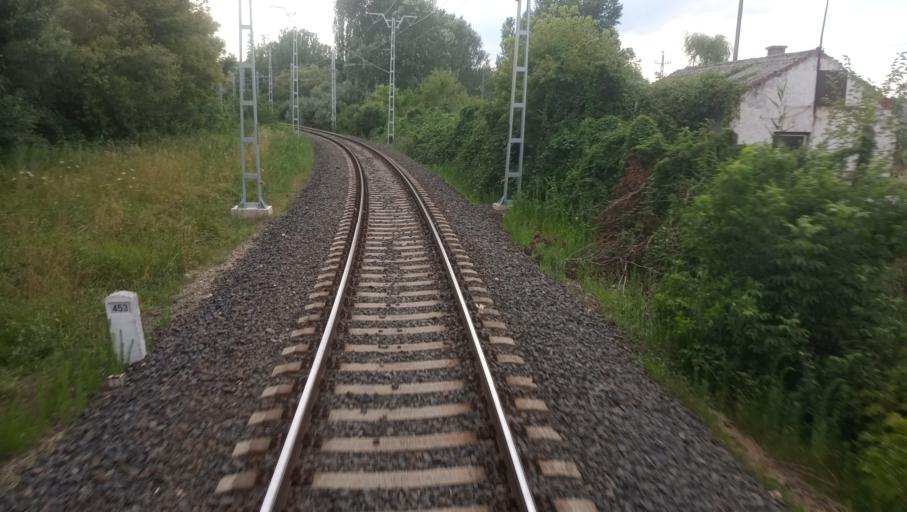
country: HU
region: Veszprem
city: Balatonalmadi
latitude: 47.0637
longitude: 18.0383
